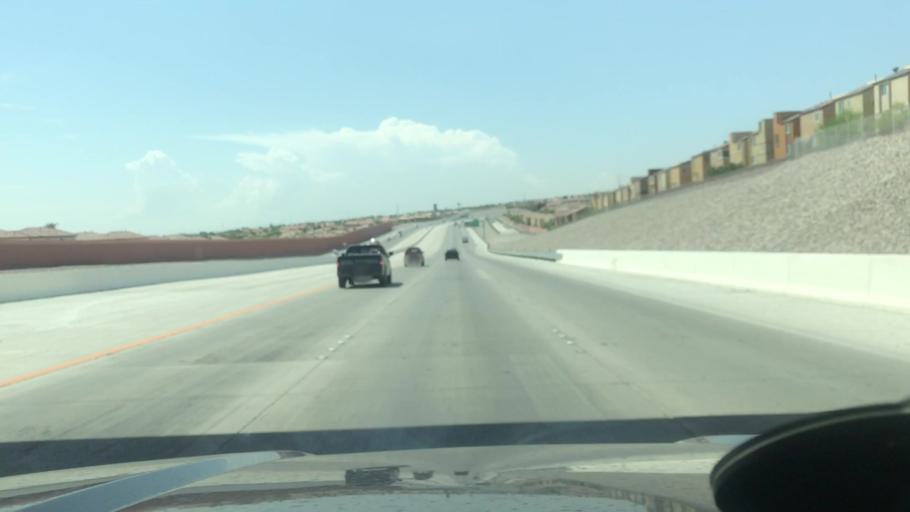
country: US
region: Nevada
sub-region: Clark County
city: Summerlin South
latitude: 36.2328
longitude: -115.3257
